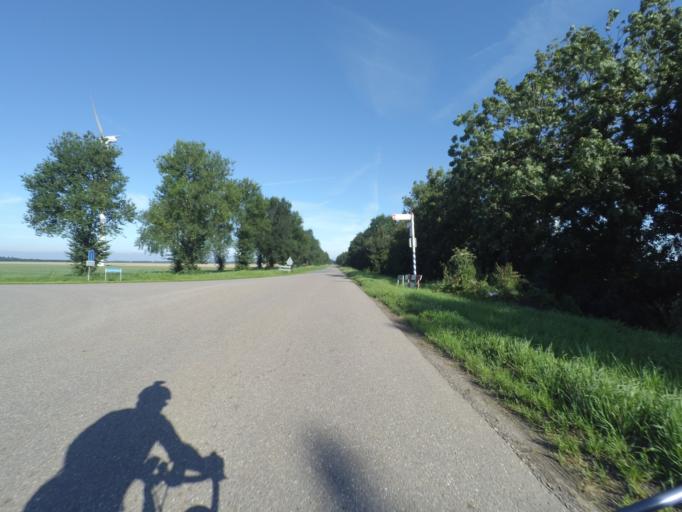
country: NL
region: Flevoland
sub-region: Gemeente Zeewolde
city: Zeewolde
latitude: 52.3819
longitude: 5.5005
